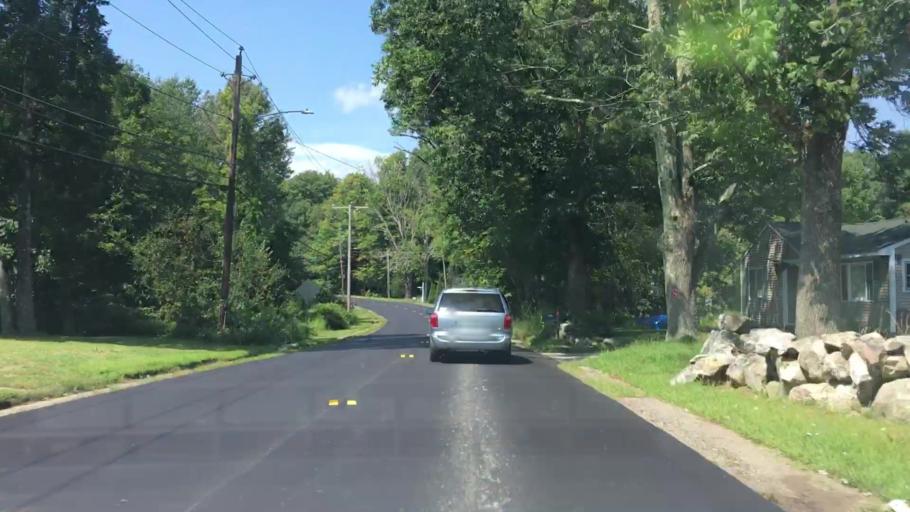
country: US
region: New Hampshire
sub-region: Rockingham County
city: Hampstead
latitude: 42.8915
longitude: -71.2040
